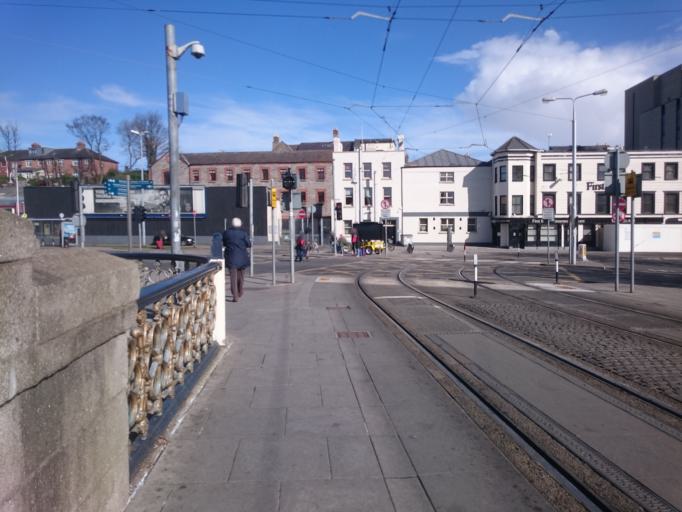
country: IE
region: Leinster
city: Rialto
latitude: 53.3477
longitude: -6.2919
